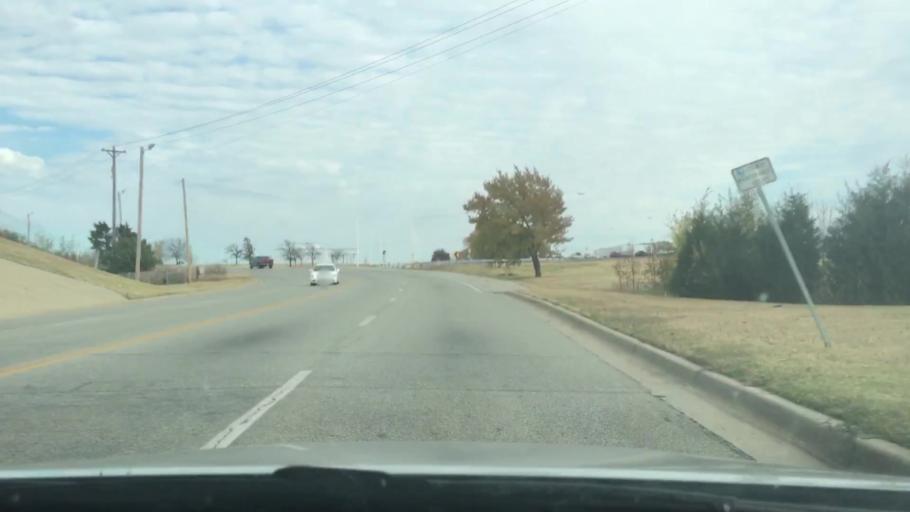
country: US
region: Kansas
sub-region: Sedgwick County
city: Wichita
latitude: 37.6500
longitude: -97.2716
